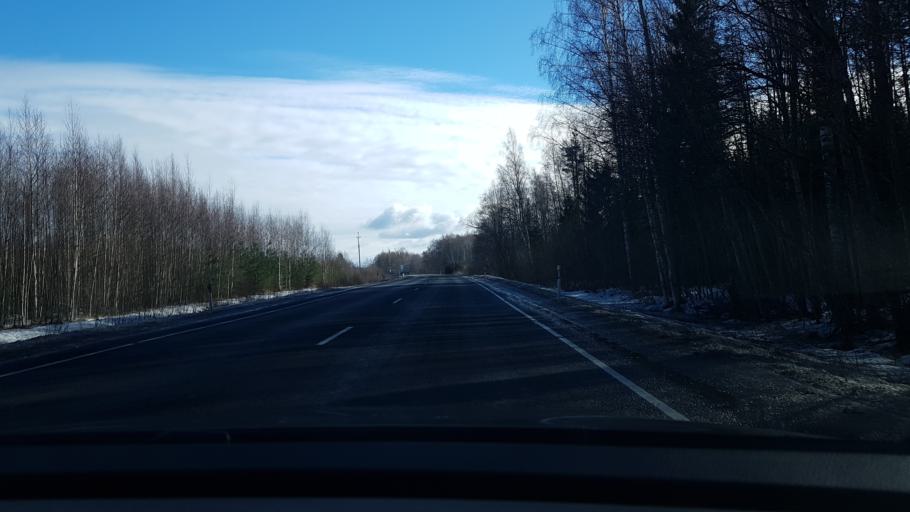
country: EE
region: Paernumaa
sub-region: Paikuse vald
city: Paikuse
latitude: 58.1950
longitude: 24.7505
